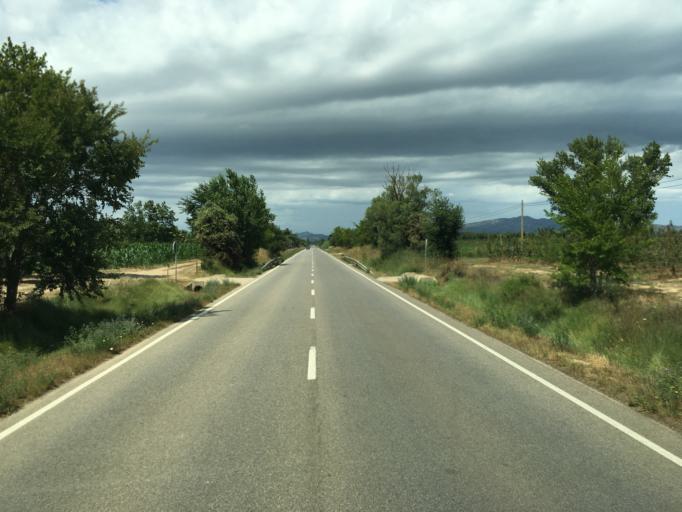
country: ES
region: Catalonia
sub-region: Provincia de Girona
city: Sant Pere Pescador
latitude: 42.1980
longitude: 3.0833
